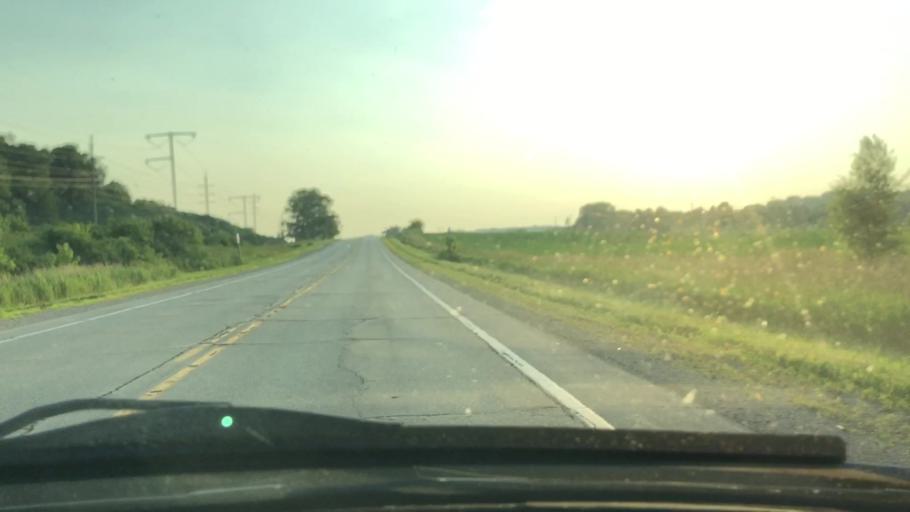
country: US
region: Wisconsin
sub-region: Dane County
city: Middleton
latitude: 43.0957
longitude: -89.5569
